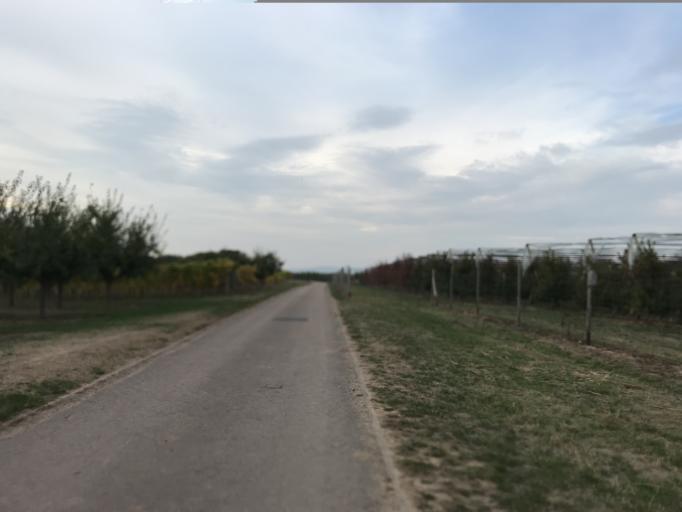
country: DE
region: Rheinland-Pfalz
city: Nieder-Ingelheim
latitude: 49.9612
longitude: 8.0813
